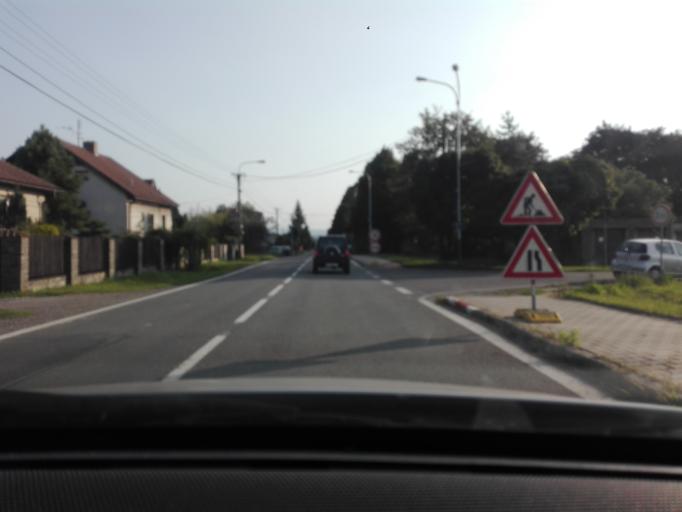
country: CZ
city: Senov
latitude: 49.8213
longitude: 18.3429
